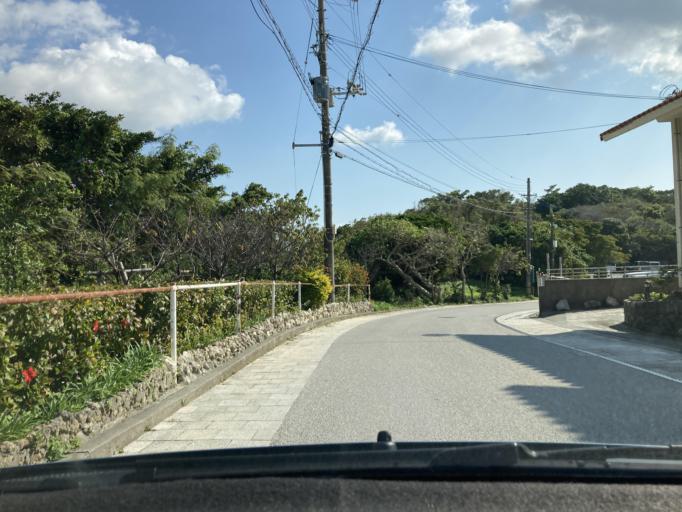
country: JP
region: Okinawa
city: Ginowan
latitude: 26.2485
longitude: 127.7297
